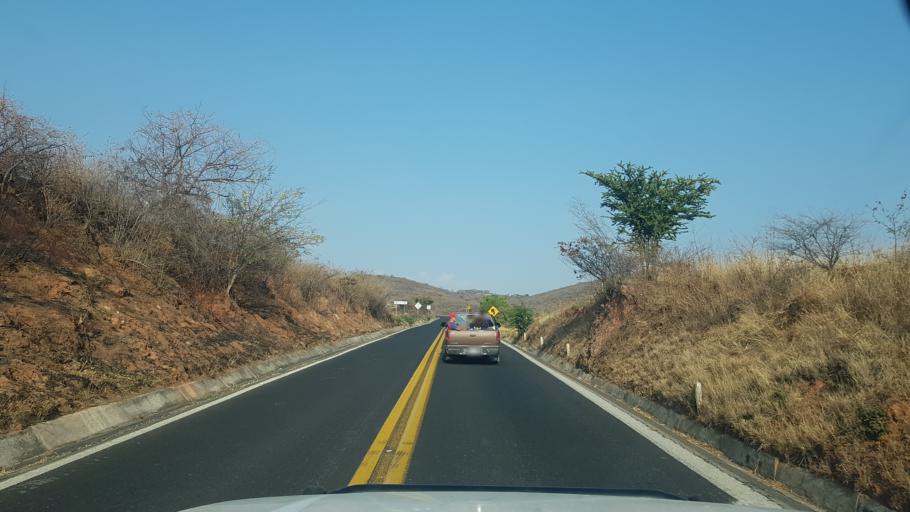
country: MX
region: Puebla
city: Calmeca
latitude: 18.6416
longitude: -98.6121
